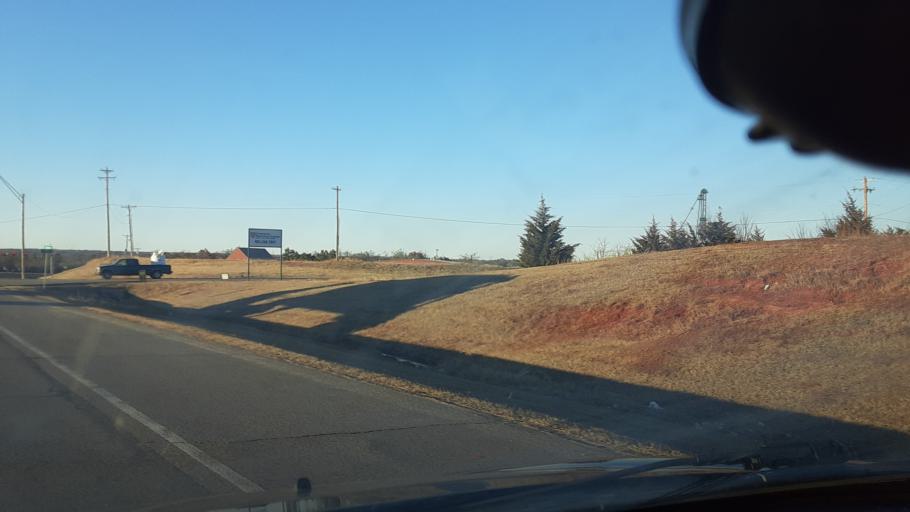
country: US
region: Oklahoma
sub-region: Logan County
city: Guthrie
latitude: 35.8261
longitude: -97.4222
